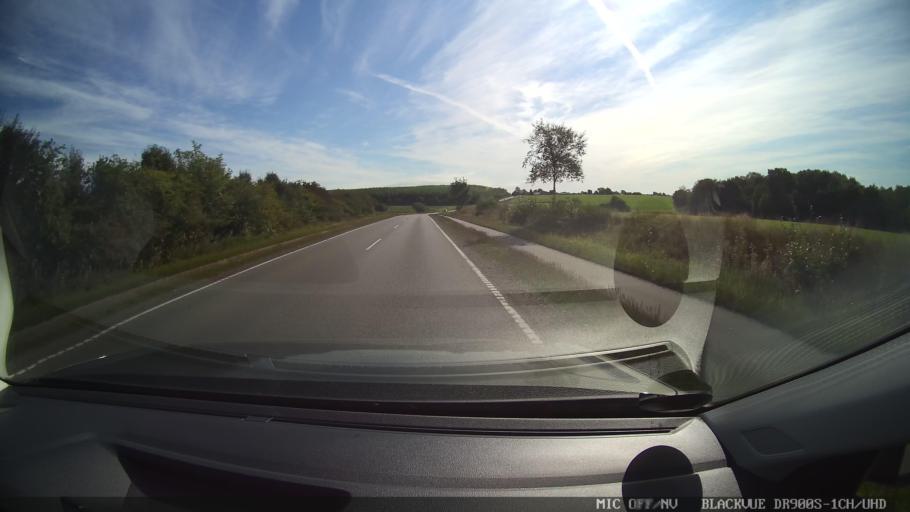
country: DK
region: North Denmark
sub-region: Mariagerfjord Kommune
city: Arden
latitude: 56.7735
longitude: 9.8412
